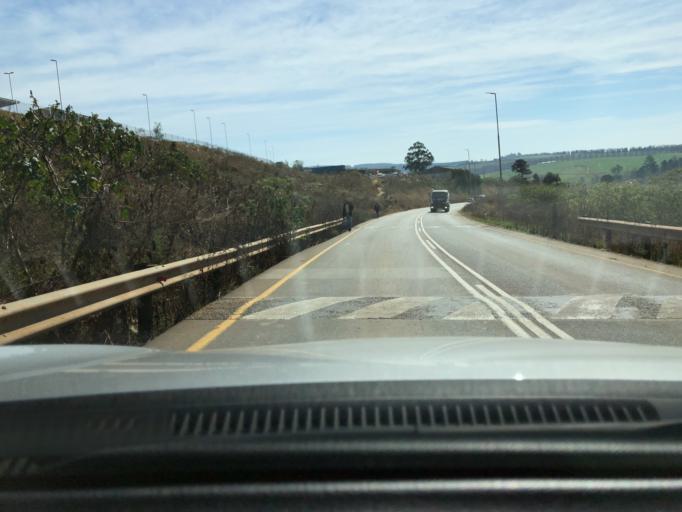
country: ZA
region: KwaZulu-Natal
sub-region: Sisonke District Municipality
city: Ixopo
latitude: -30.1513
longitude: 30.0657
